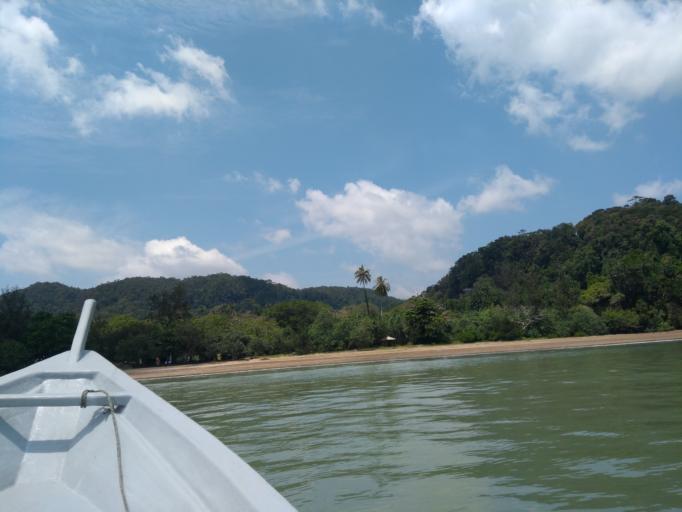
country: MY
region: Sarawak
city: Kuching
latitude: 1.7177
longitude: 110.4429
